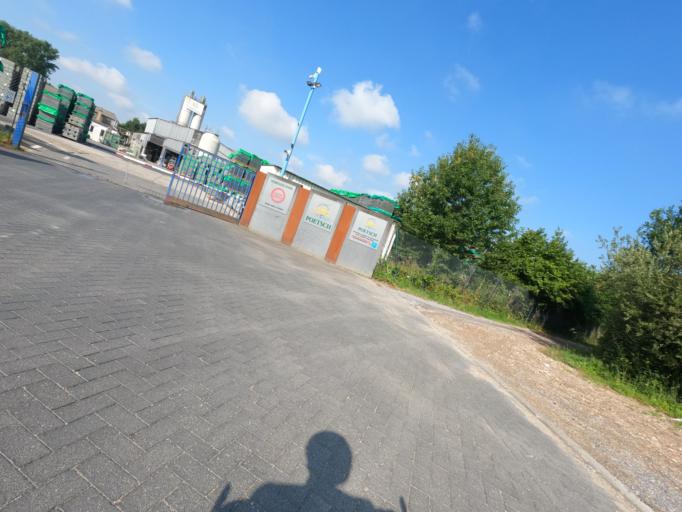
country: DE
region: North Rhine-Westphalia
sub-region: Regierungsbezirk Koln
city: Heinsberg
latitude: 51.0823
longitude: 6.0804
